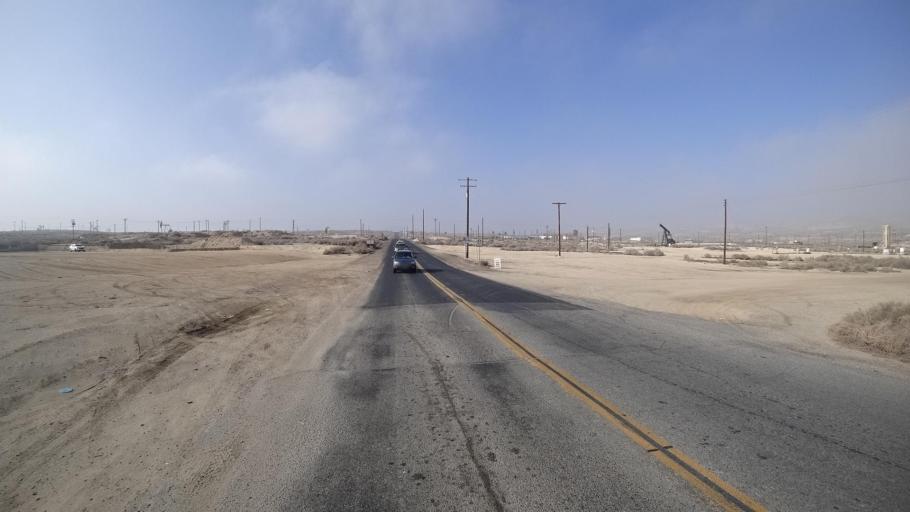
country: US
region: California
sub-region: Kern County
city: Ford City
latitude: 35.1805
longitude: -119.4545
